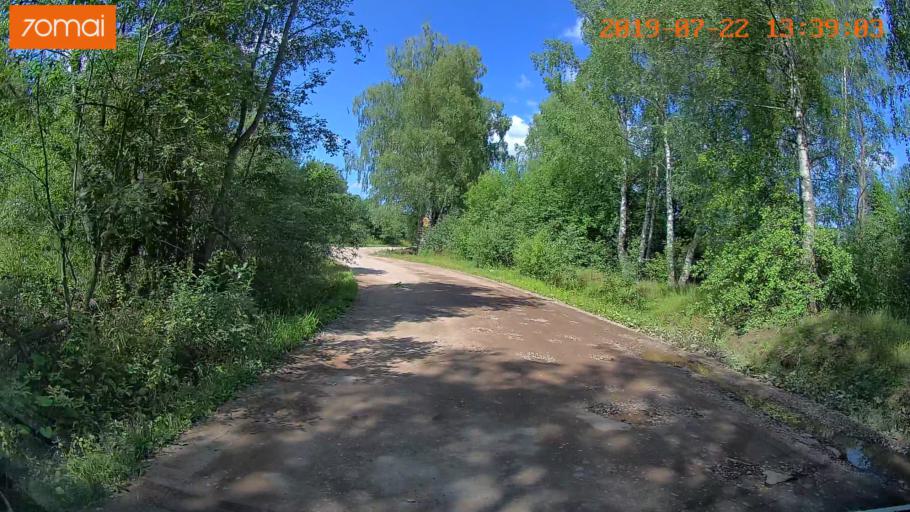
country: RU
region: Ivanovo
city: Novo-Talitsy
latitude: 57.0715
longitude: 40.8820
